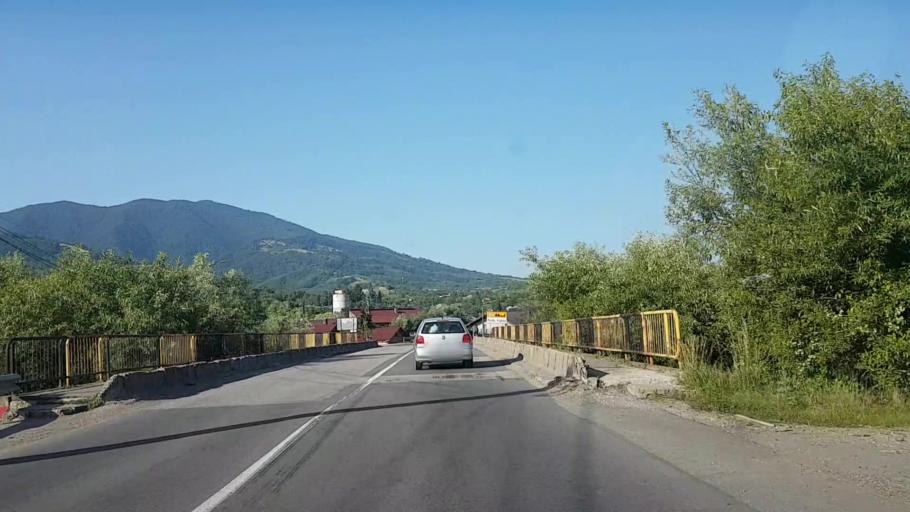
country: RO
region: Bistrita-Nasaud
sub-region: Comuna Prundu Bargaului
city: Susenii Bargaului
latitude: 47.2196
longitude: 24.7175
